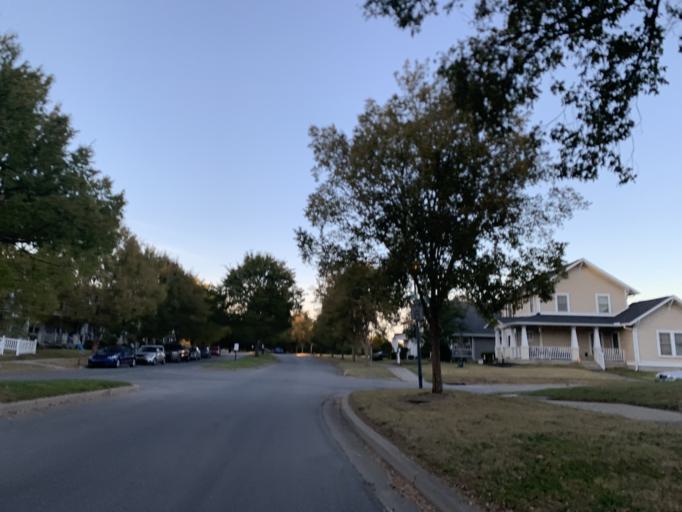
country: US
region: Kentucky
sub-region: Jefferson County
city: Shively
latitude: 38.2261
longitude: -85.8184
